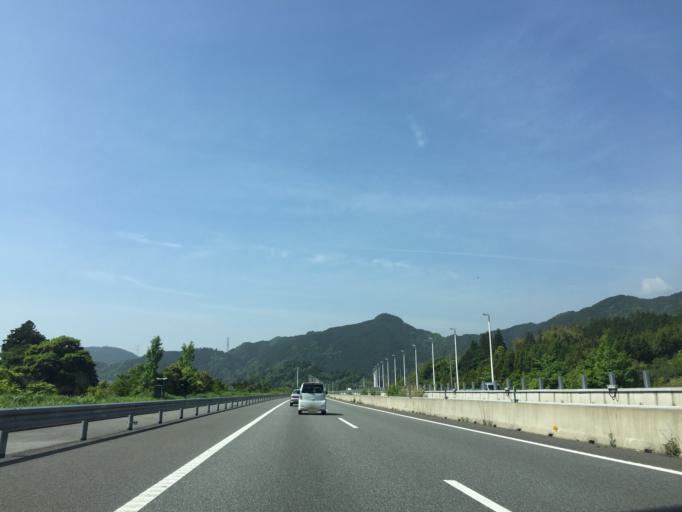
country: JP
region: Shizuoka
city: Fujinomiya
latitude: 35.1376
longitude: 138.5151
